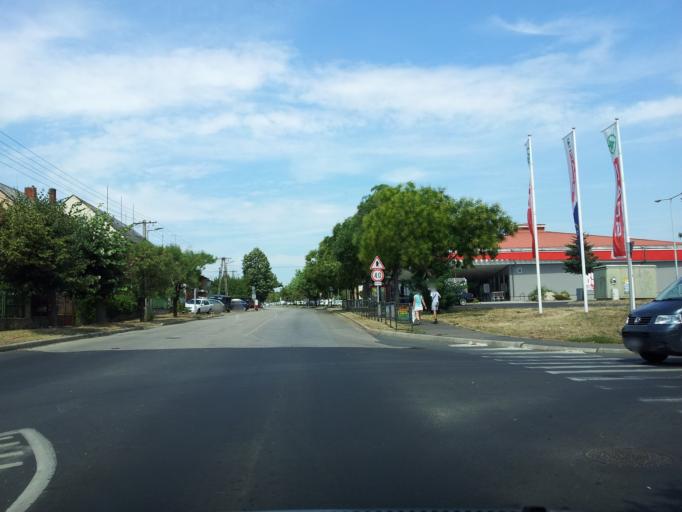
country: HU
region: Veszprem
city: Tapolca
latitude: 46.8849
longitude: 17.4484
